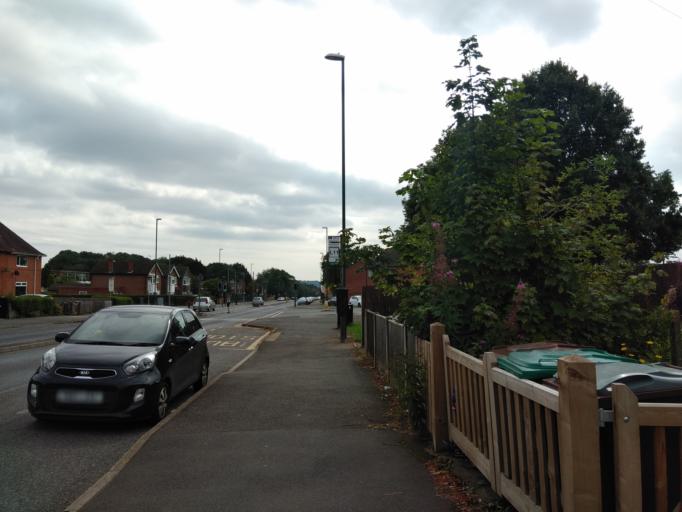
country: GB
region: England
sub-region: Nottinghamshire
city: Kimberley
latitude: 52.9692
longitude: -1.2117
